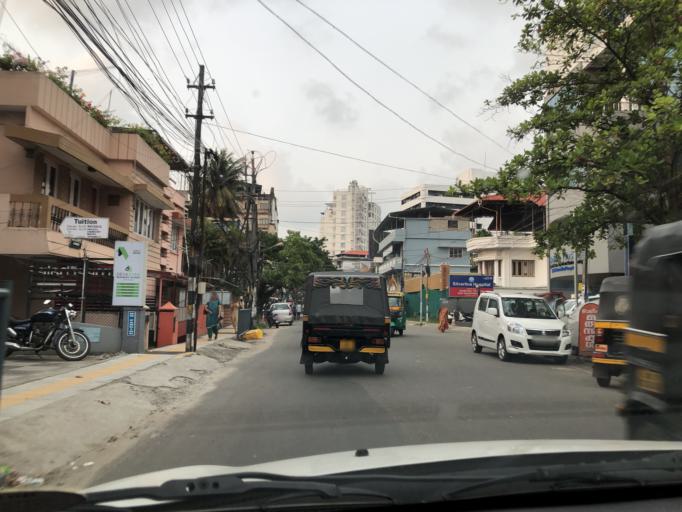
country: IN
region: Kerala
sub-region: Ernakulam
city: Cochin
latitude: 9.9650
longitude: 76.3002
